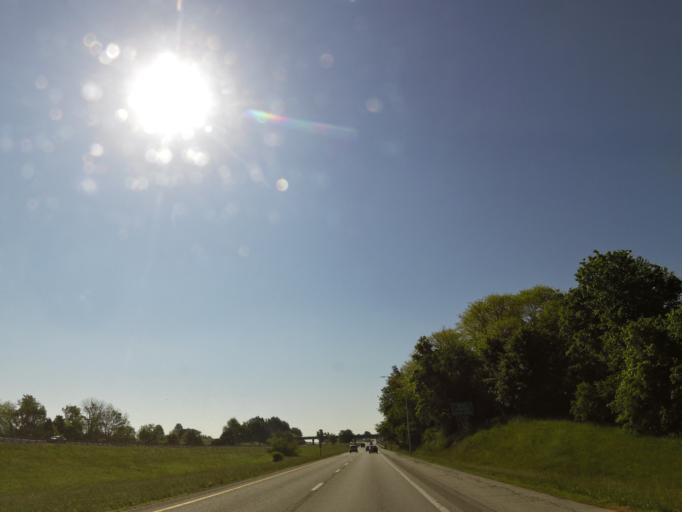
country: US
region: Kentucky
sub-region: Shelby County
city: Shelbyville
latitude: 38.1748
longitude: -85.1638
